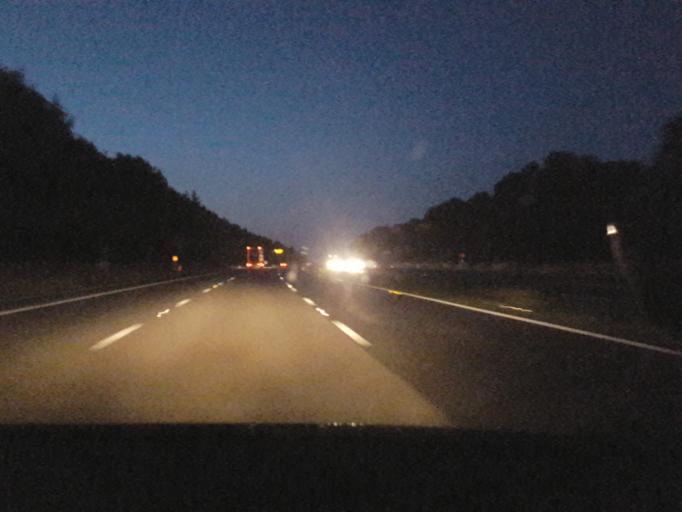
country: GB
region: England
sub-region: Leicestershire
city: Shepshed
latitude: 52.7364
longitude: -1.2816
